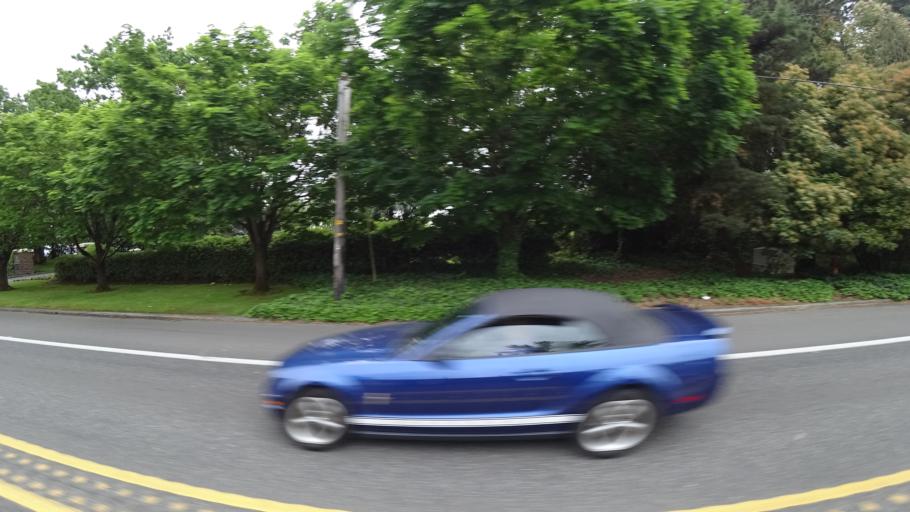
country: US
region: Washington
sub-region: Clark County
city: Vancouver
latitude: 45.6005
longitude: -122.6424
